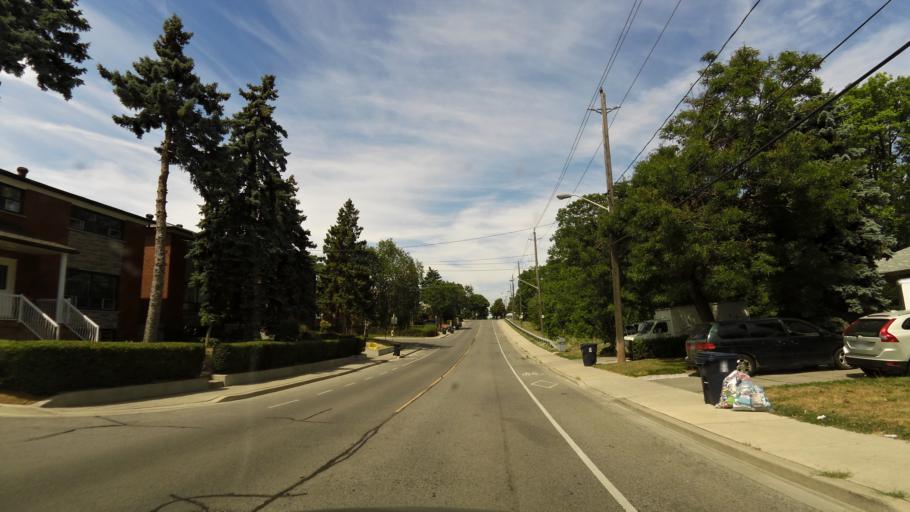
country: CA
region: Ontario
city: Etobicoke
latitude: 43.6336
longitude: -79.4856
